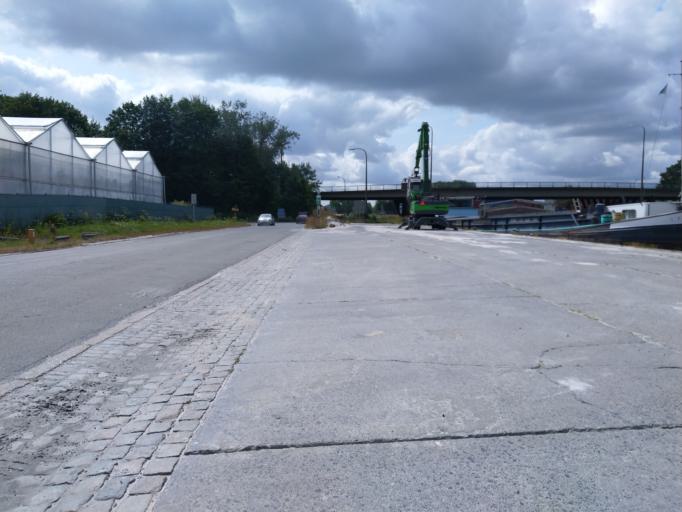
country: BE
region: Wallonia
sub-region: Province du Hainaut
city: Quaregnon
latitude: 50.4795
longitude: 3.8801
